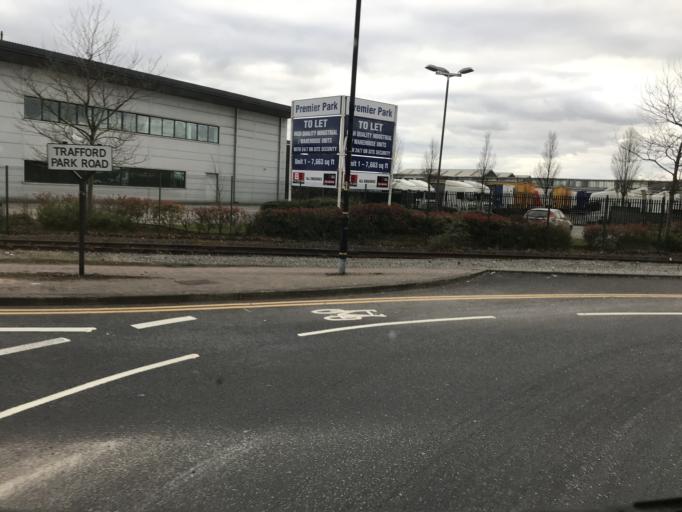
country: GB
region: England
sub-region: Trafford
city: Trafford Park
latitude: 53.4716
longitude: -2.3148
